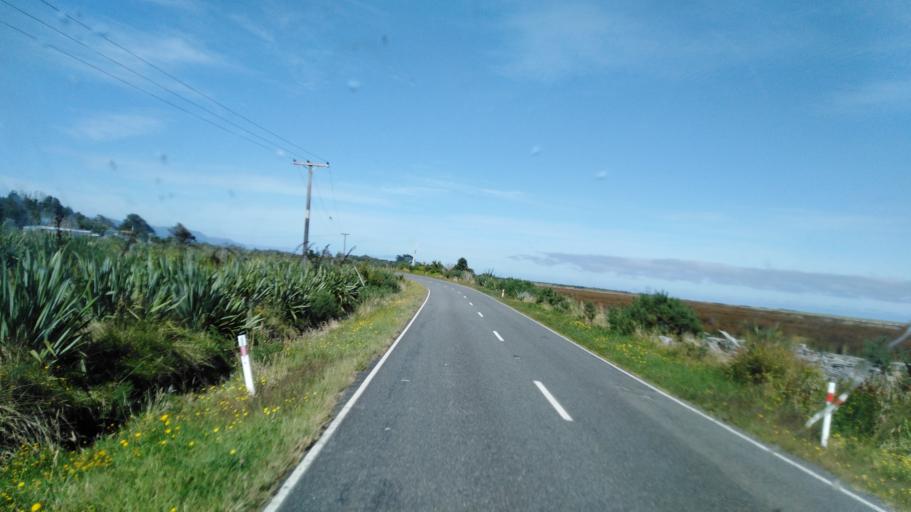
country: NZ
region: West Coast
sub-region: Buller District
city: Westport
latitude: -41.2824
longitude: 172.1055
